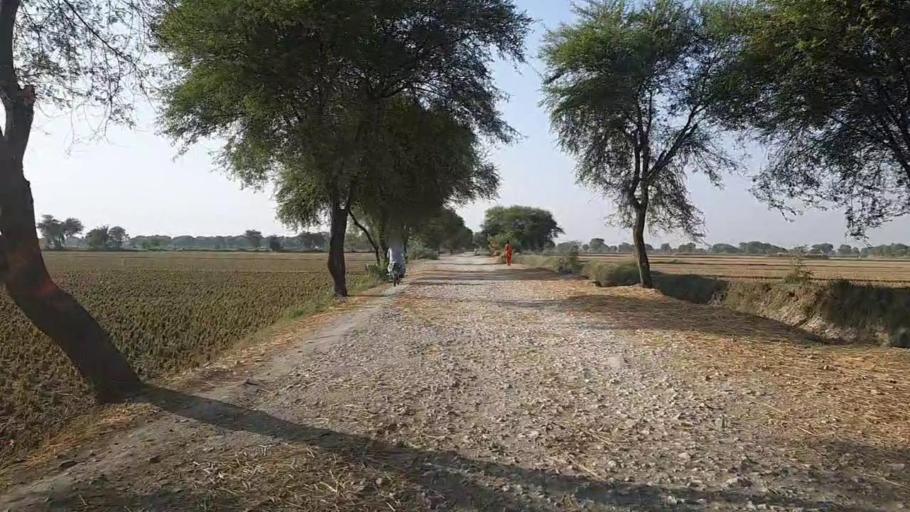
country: PK
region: Sindh
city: Kashmor
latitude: 28.4036
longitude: 69.4171
